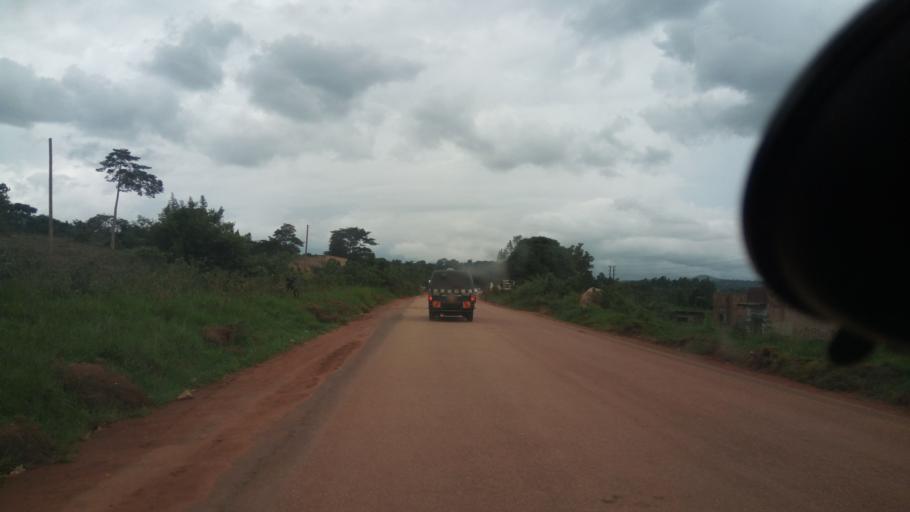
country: UG
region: Central Region
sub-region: Nakaseke District
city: Namasuba
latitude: 0.5452
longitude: 32.2340
